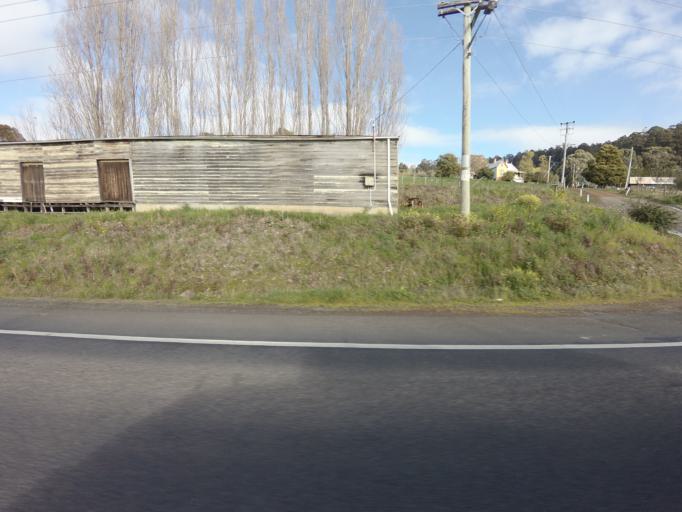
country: AU
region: Tasmania
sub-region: Huon Valley
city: Franklin
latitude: -43.1075
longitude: 147.0006
